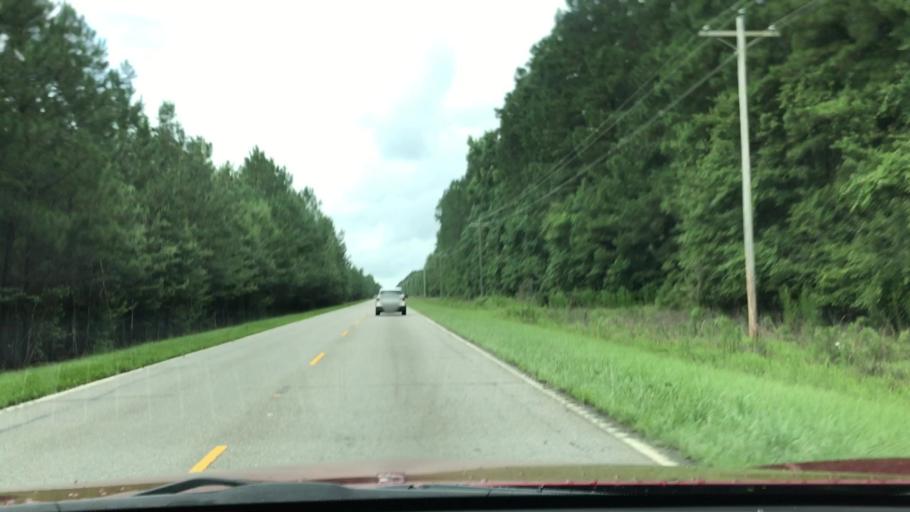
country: US
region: South Carolina
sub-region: Georgetown County
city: Murrells Inlet
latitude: 33.5969
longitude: -79.2019
